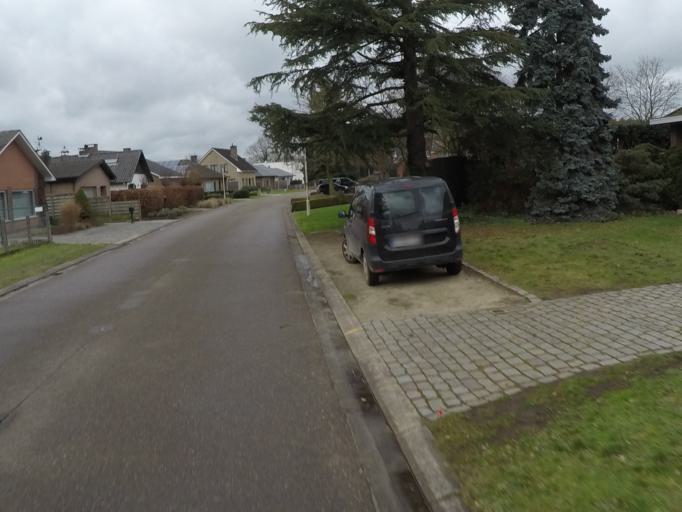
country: BE
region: Flanders
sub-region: Provincie Antwerpen
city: Zandhoven
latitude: 51.2178
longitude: 4.6547
